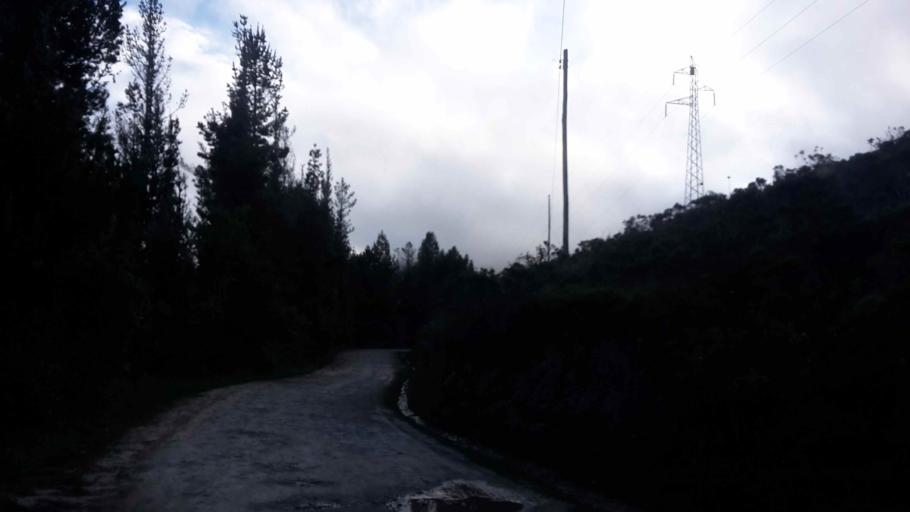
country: BO
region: Cochabamba
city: Colomi
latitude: -17.2386
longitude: -65.9020
